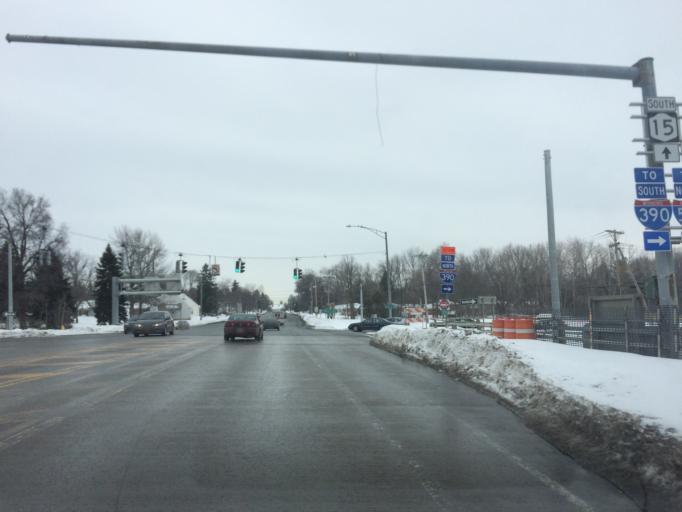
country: US
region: New York
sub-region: Monroe County
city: Rochester
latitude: 43.1123
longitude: -77.6237
